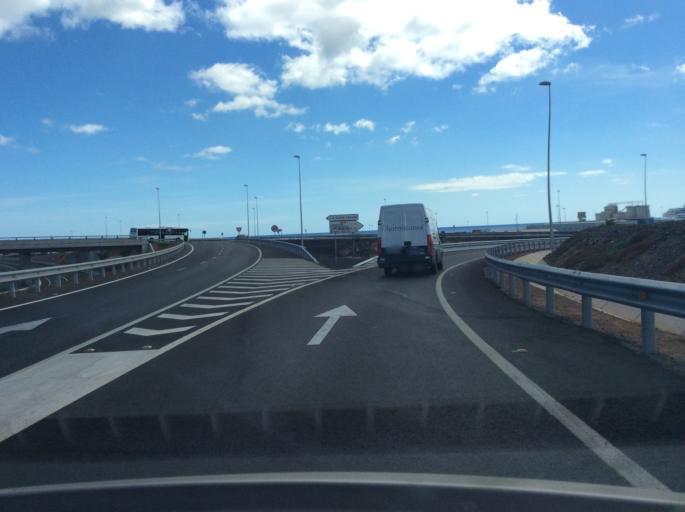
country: ES
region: Canary Islands
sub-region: Provincia de Las Palmas
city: Arrecife
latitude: 28.9776
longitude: -13.5330
